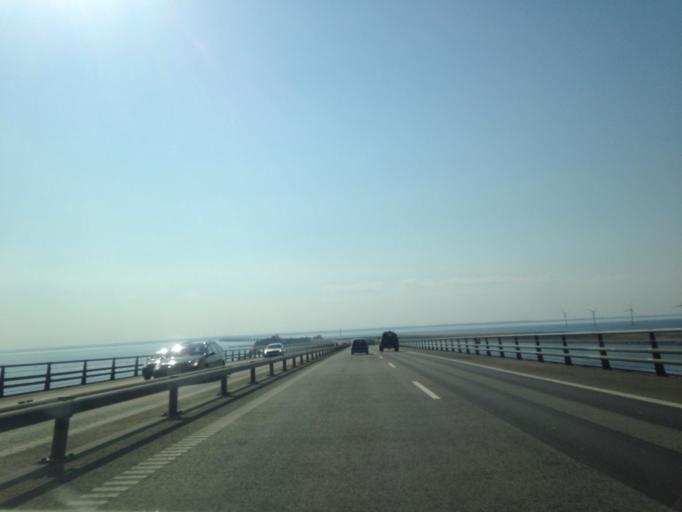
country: DK
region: Zealand
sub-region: Slagelse Kommune
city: Korsor
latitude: 55.3379
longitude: 11.0032
